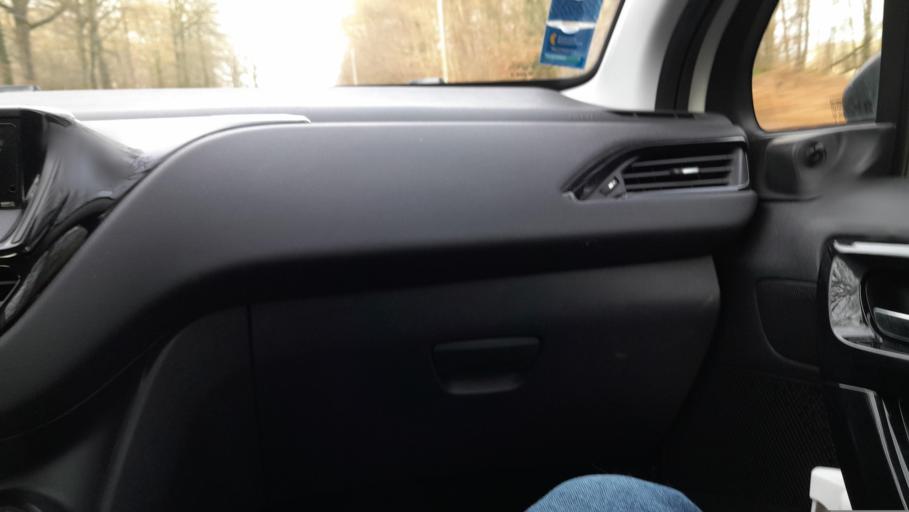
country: FR
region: Brittany
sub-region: Departement d'Ille-et-Vilaine
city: La Guerche-de-Bretagne
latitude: 47.9100
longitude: -1.1951
